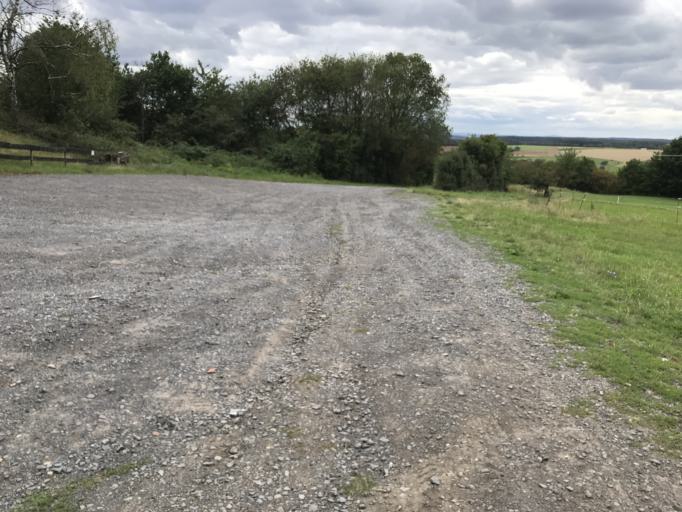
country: DE
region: Hesse
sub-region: Regierungsbezirk Giessen
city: Laubach
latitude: 50.5645
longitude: 8.9718
